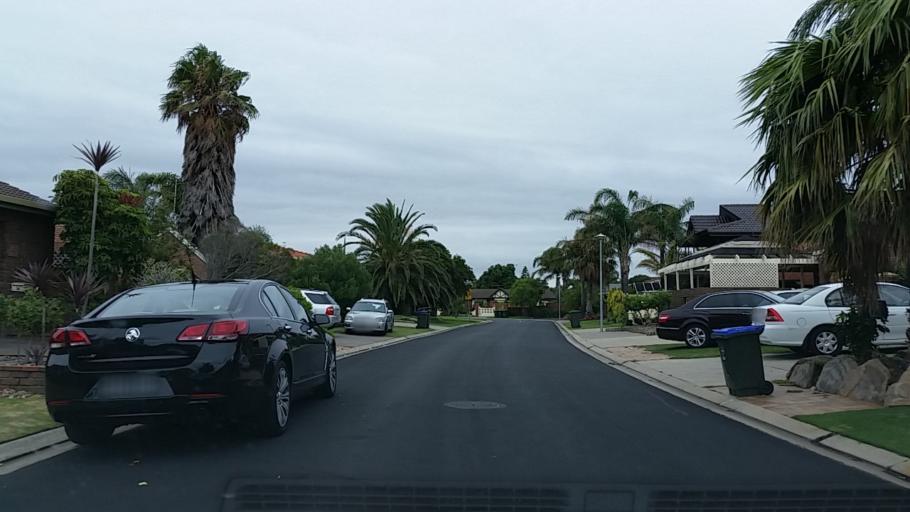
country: AU
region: South Australia
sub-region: Charles Sturt
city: West Lakes Shore
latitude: -34.8759
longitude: 138.4891
